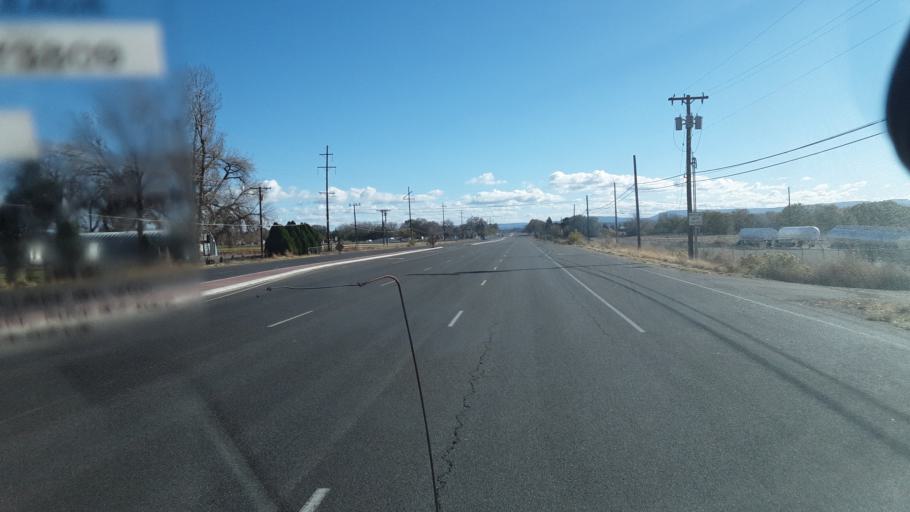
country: US
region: New Mexico
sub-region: San Juan County
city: Lee Acres
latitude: 36.7009
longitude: -108.0527
